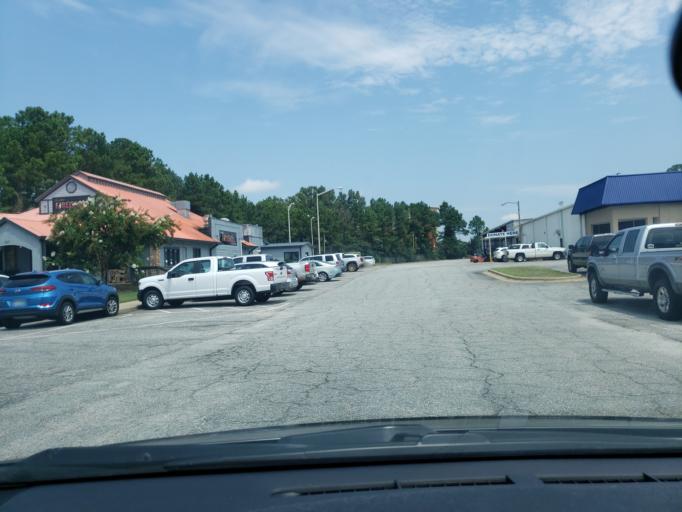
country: US
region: Georgia
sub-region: Dougherty County
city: Albany
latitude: 31.6137
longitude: -84.2214
